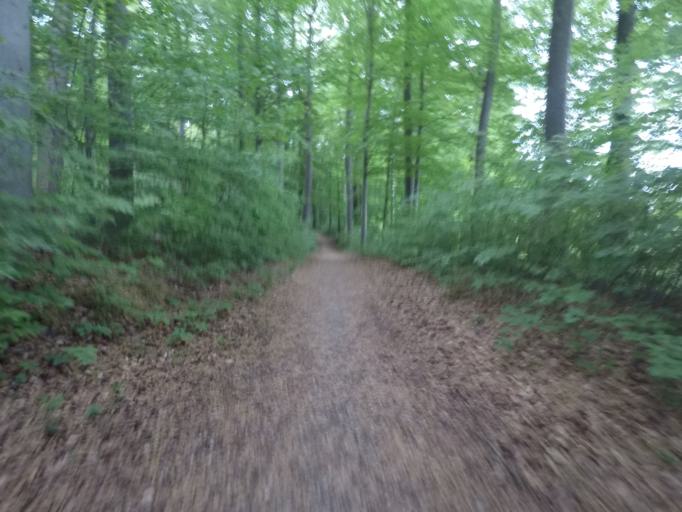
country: DE
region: North Rhine-Westphalia
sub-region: Regierungsbezirk Detmold
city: Bad Salzuflen
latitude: 52.1049
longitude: 8.7557
